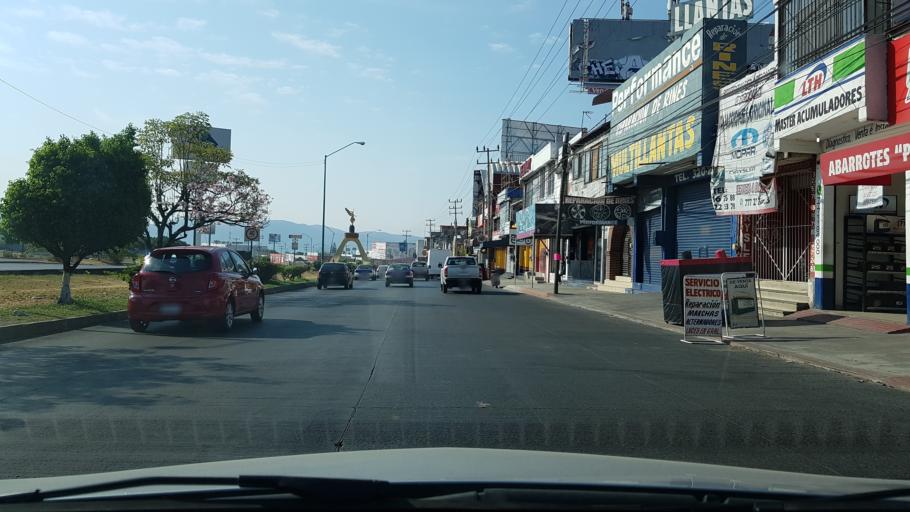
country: MX
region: Morelos
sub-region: Tepoztlan
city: Tetecolala
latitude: 18.9098
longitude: -99.1808
